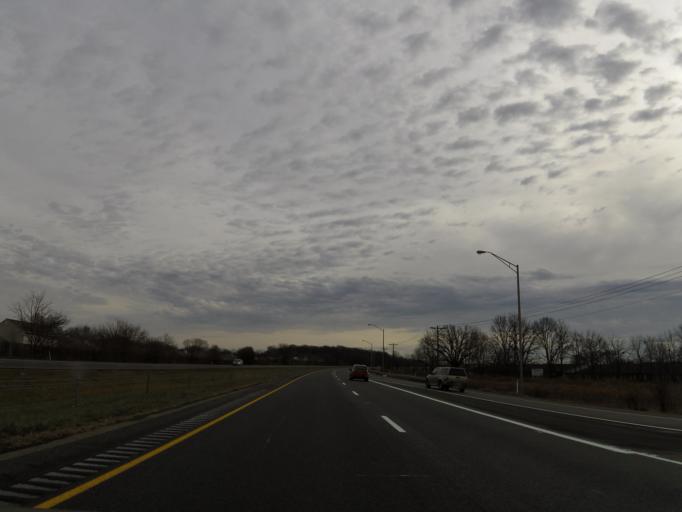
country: US
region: Indiana
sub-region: Hendricks County
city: Brownsburg
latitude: 39.8594
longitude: -86.3905
